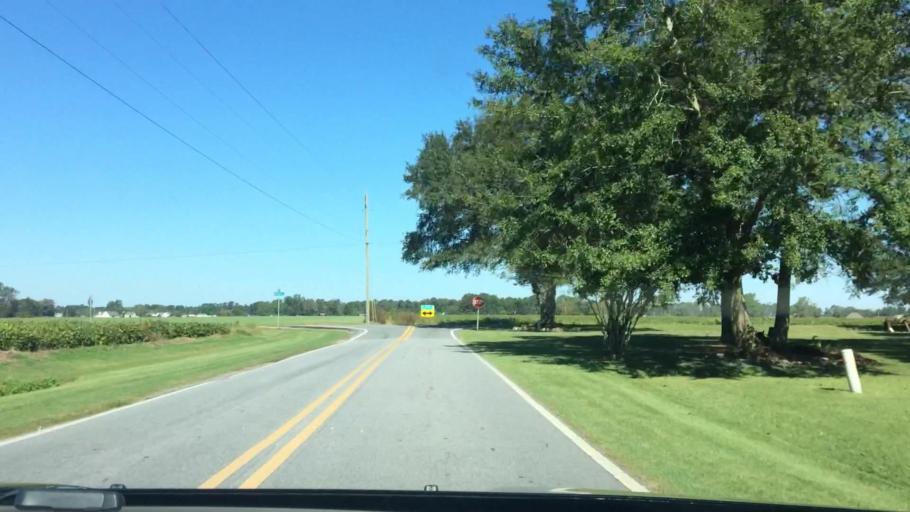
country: US
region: North Carolina
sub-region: Pitt County
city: Winterville
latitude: 35.5201
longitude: -77.4333
